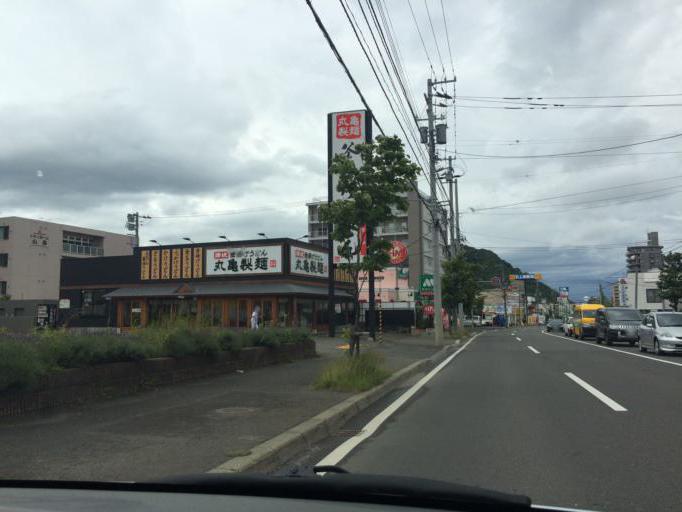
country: JP
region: Hokkaido
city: Sapporo
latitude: 43.0367
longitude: 141.3313
